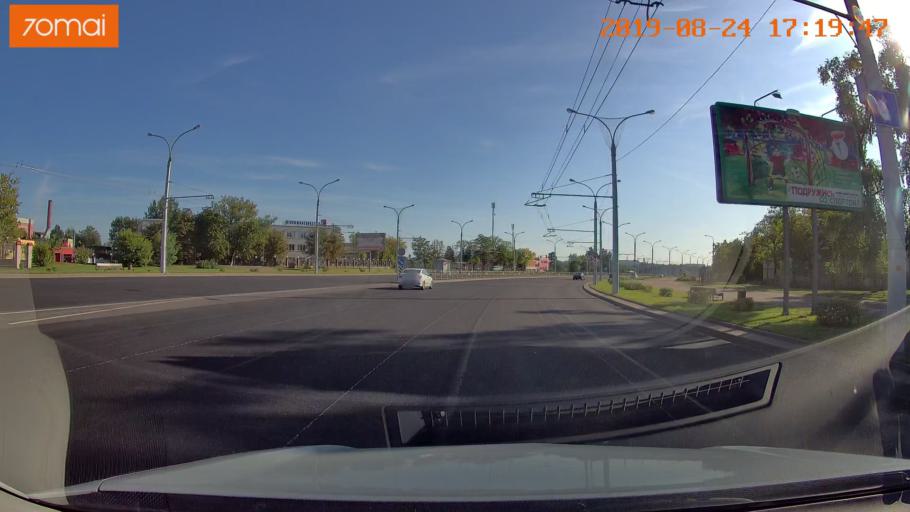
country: BY
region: Minsk
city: Vyaliki Trastsyanets
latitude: 53.8587
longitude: 27.6404
